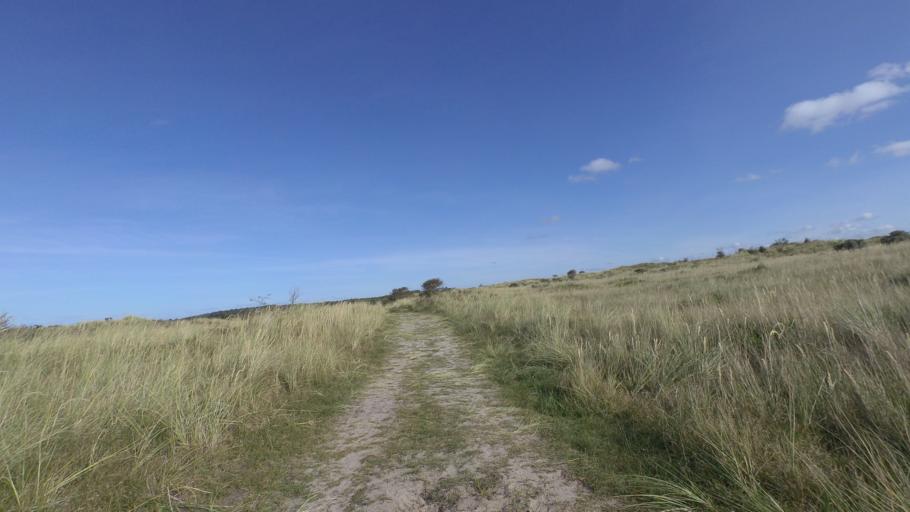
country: NL
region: Friesland
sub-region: Gemeente Ameland
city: Nes
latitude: 53.4503
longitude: 5.7423
